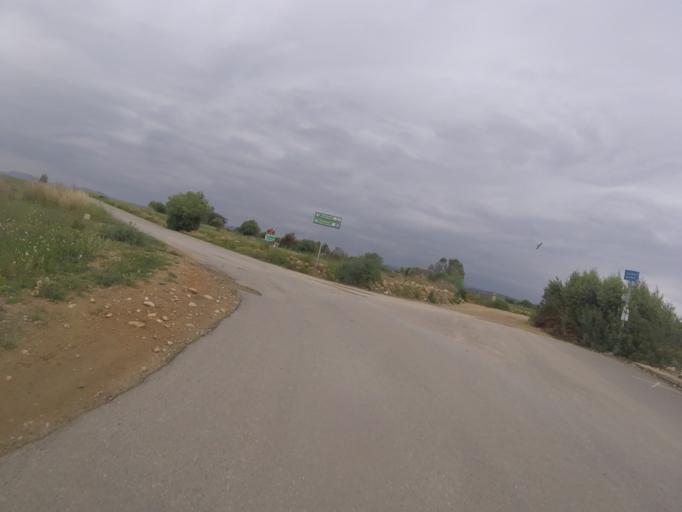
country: ES
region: Valencia
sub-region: Provincia de Castello
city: Torreblanca
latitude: 40.2139
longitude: 0.2464
